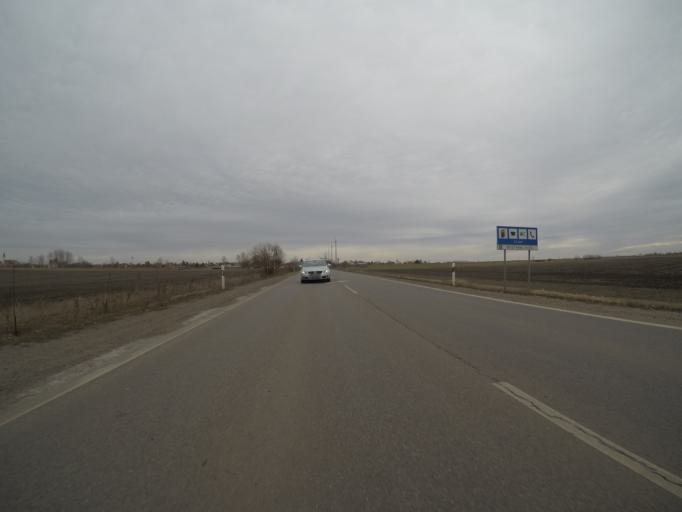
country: HU
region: Jasz-Nagykun-Szolnok
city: Jaszjakohalma
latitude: 47.5202
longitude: 19.9758
